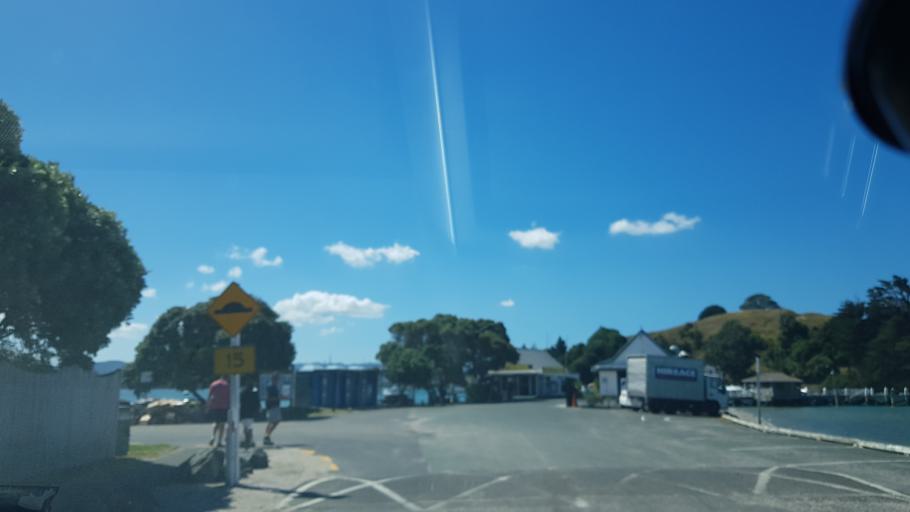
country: NZ
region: Auckland
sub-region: Auckland
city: Warkworth
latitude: -36.3899
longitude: 174.7291
